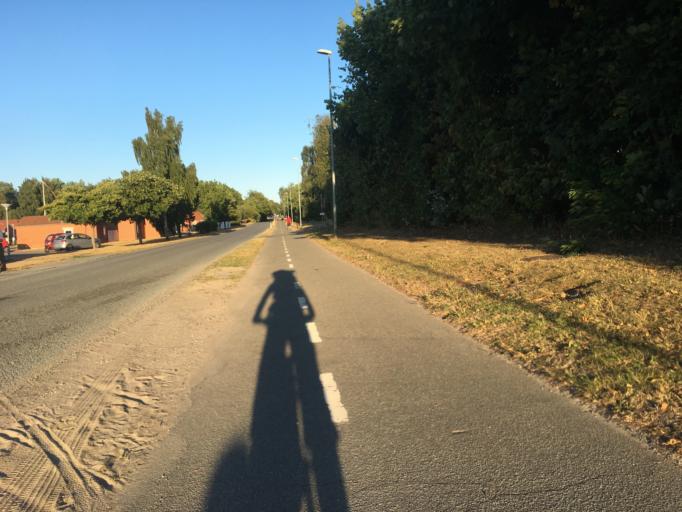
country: DK
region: Central Jutland
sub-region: Syddjurs Kommune
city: Hornslet
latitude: 56.3144
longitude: 10.3235
